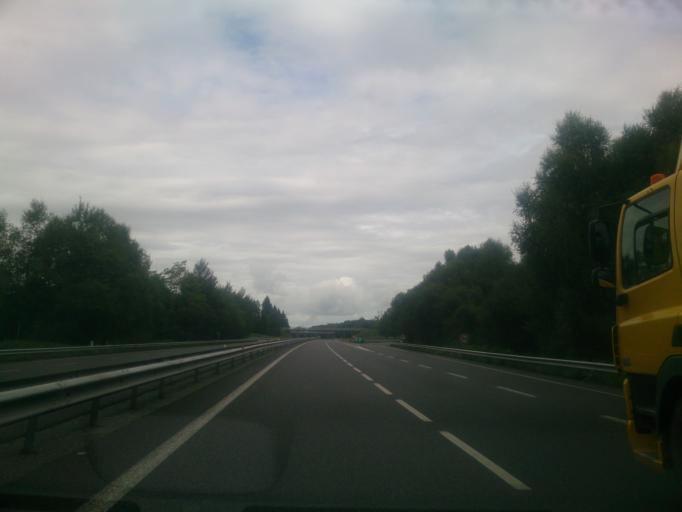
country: FR
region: Midi-Pyrenees
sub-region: Departement des Hautes-Pyrenees
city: La Barthe-de-Neste
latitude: 43.0995
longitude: 0.3950
